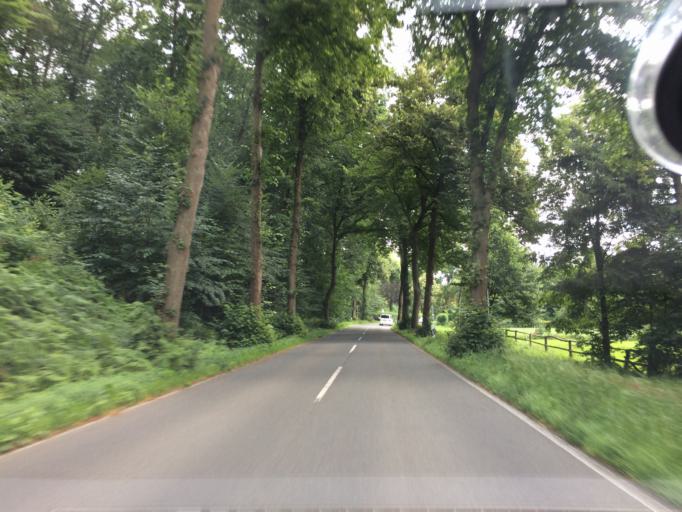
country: DE
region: North Rhine-Westphalia
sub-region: Regierungsbezirk Munster
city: Haltern
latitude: 51.7311
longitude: 7.1613
